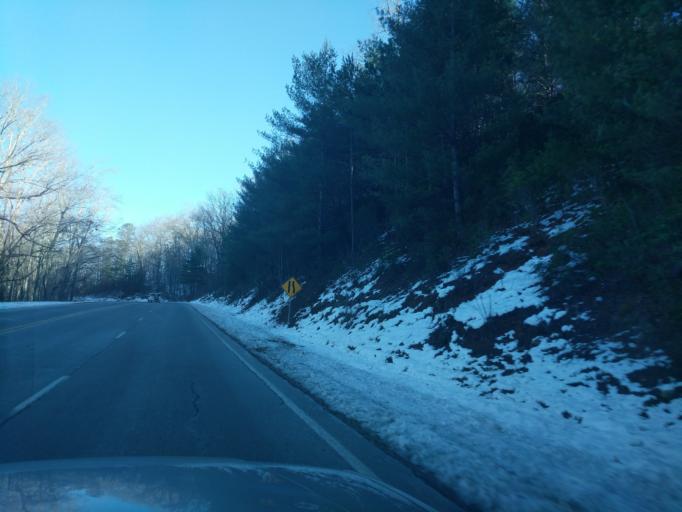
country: US
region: Georgia
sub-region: Rabun County
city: Clayton
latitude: 34.8722
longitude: -83.5617
